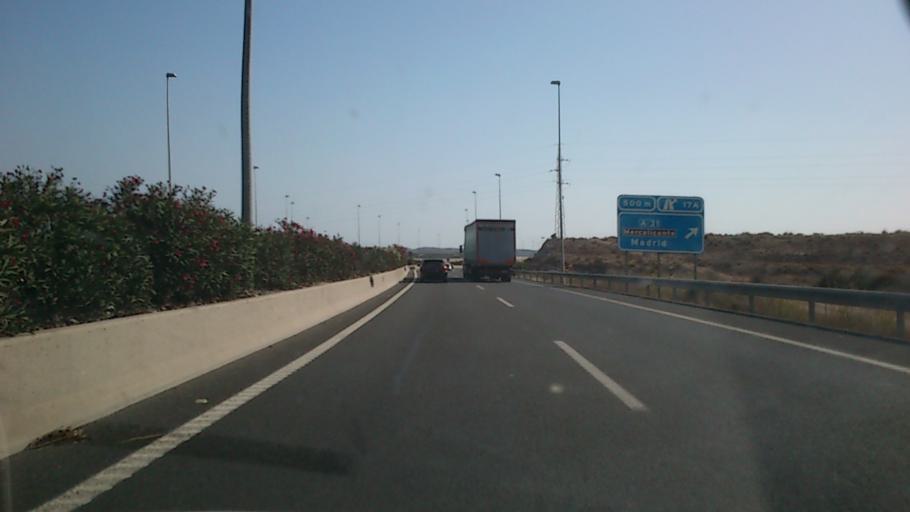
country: ES
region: Valencia
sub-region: Provincia de Alicante
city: San Vicent del Raspeig
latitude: 38.3474
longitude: -0.5413
